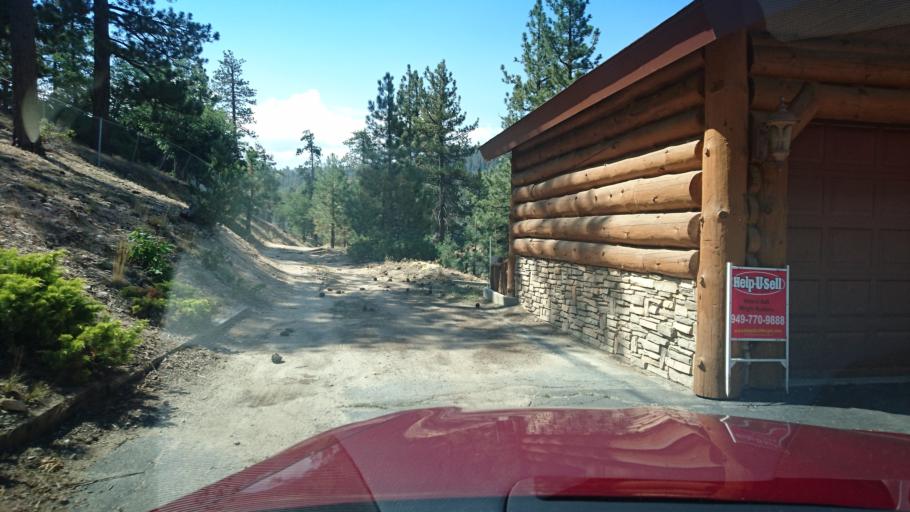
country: US
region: California
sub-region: San Bernardino County
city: Big Bear Lake
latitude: 34.2409
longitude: -116.9485
